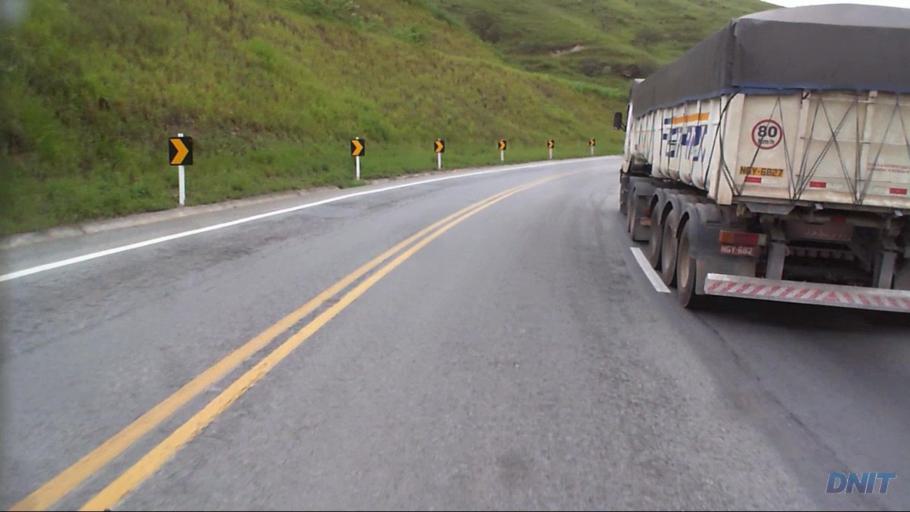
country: BR
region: Minas Gerais
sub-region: Nova Era
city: Nova Era
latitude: -19.6499
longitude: -42.9337
